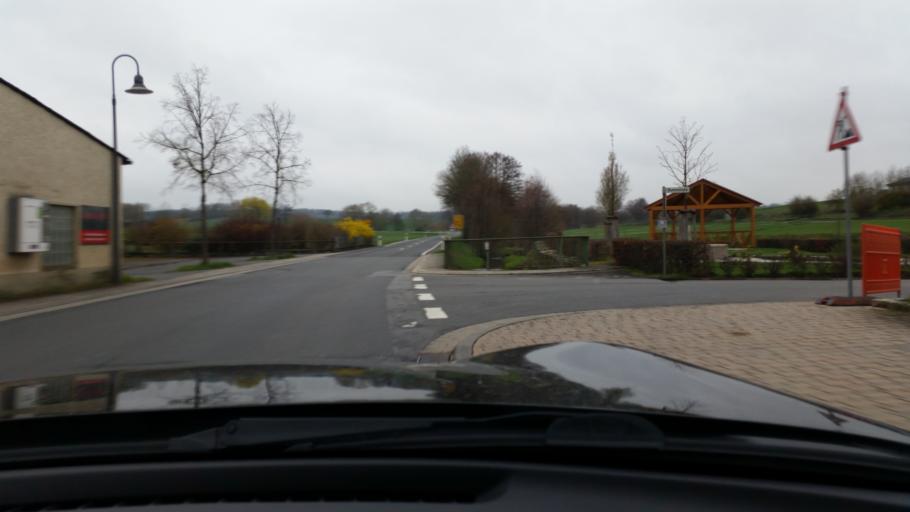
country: DE
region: Baden-Wuerttemberg
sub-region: Karlsruhe Region
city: Osterburken
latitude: 49.4740
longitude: 9.4096
